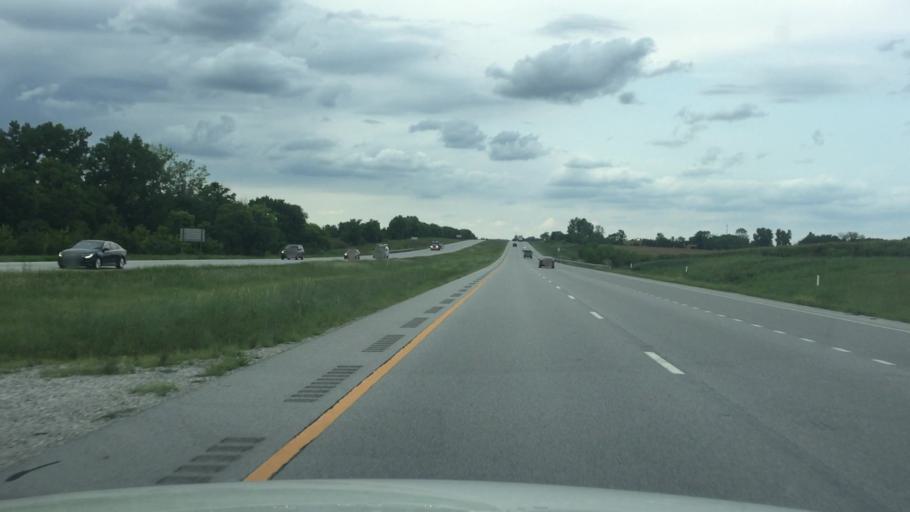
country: US
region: Kansas
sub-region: Miami County
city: Louisburg
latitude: 38.7262
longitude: -94.6764
